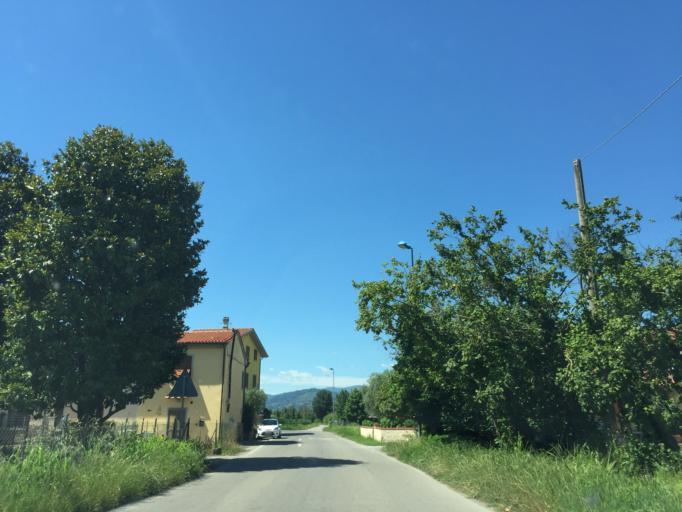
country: IT
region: Tuscany
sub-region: Provincia di Pistoia
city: Anchione
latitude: 43.8295
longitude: 10.7578
